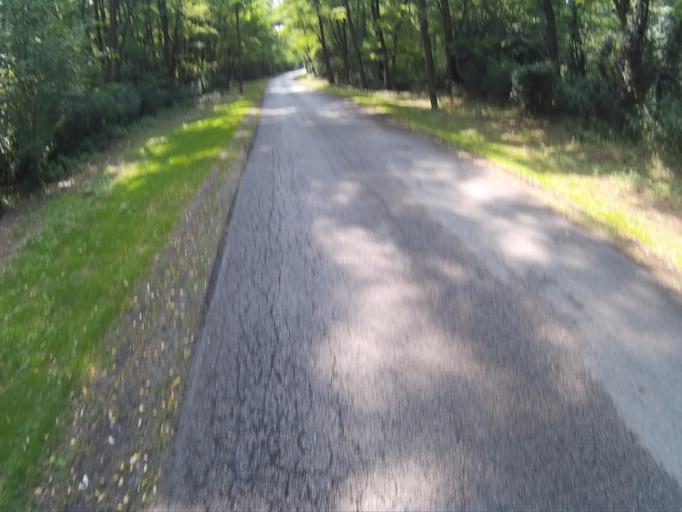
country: HU
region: Veszprem
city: Papa
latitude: 47.2841
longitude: 17.5799
